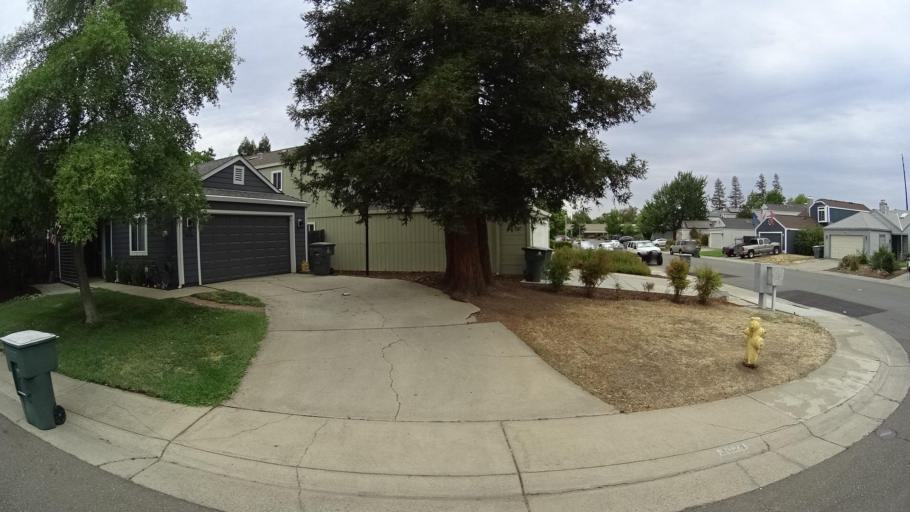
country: US
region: California
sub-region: Placer County
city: Rocklin
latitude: 38.7771
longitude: -121.2510
